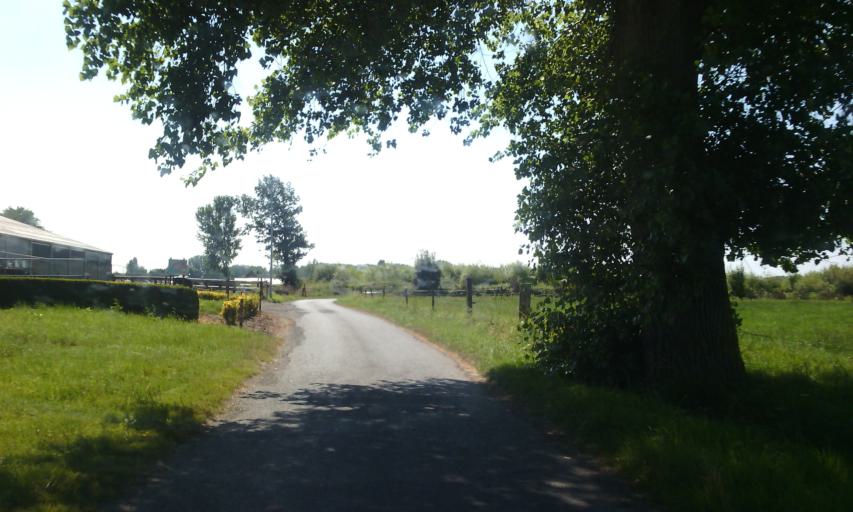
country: BE
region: Flanders
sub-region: Provincie Oost-Vlaanderen
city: Wichelen
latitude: 50.9977
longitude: 4.0049
